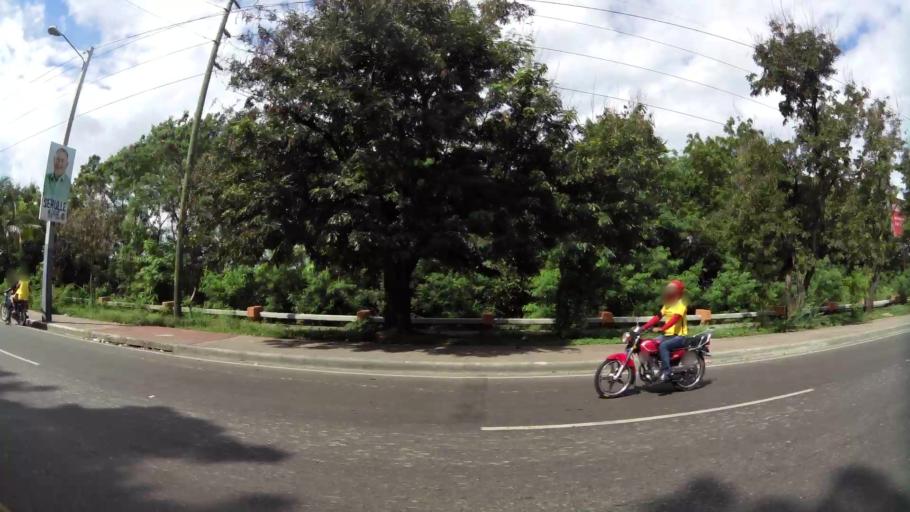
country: DO
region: Santiago
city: Santiago de los Caballeros
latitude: 19.4674
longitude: -70.7139
